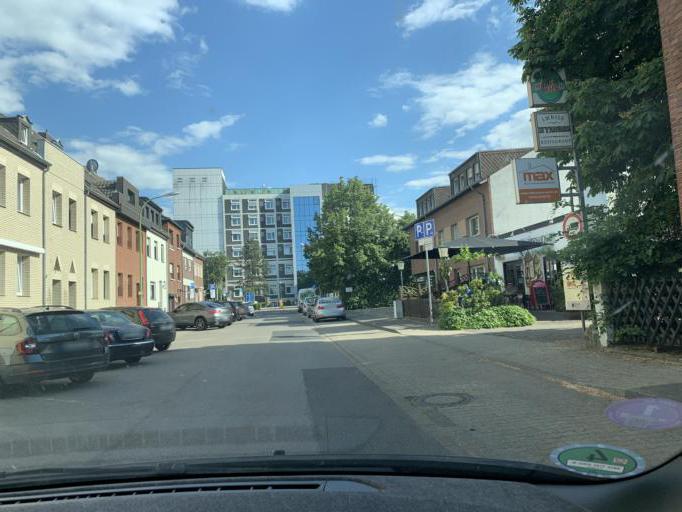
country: DE
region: North Rhine-Westphalia
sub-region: Regierungsbezirk Koln
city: Dueren
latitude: 50.8236
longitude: 6.4659
